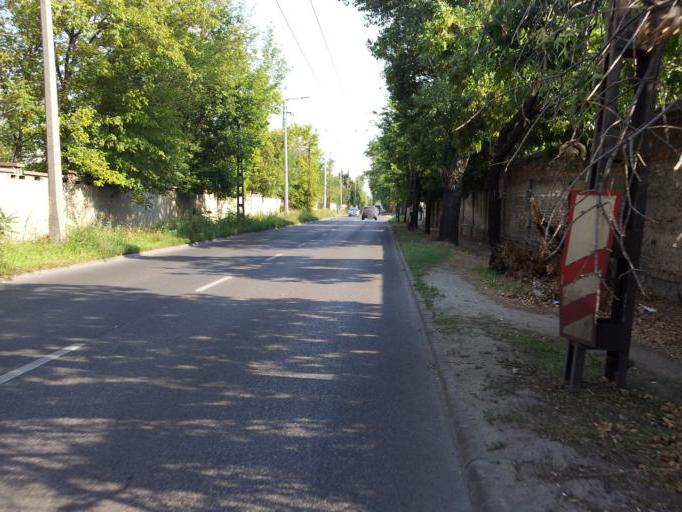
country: HU
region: Budapest
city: Budapest XIV. keruelet
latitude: 47.4965
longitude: 19.1164
